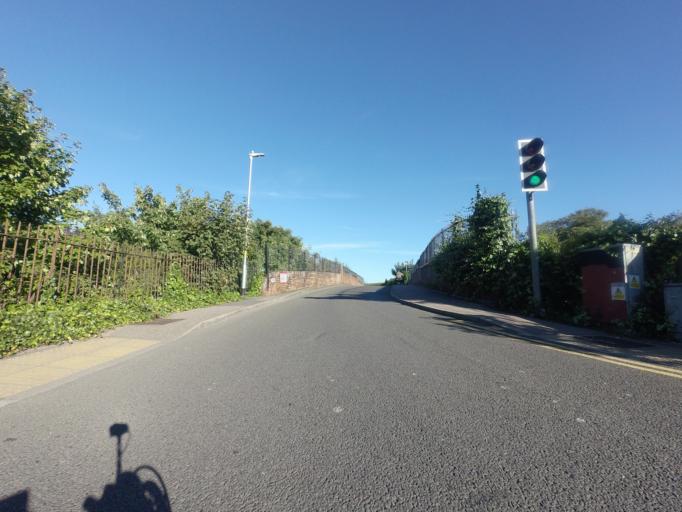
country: GB
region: England
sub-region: Kent
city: Herne Bay
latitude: 51.3643
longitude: 1.1136
